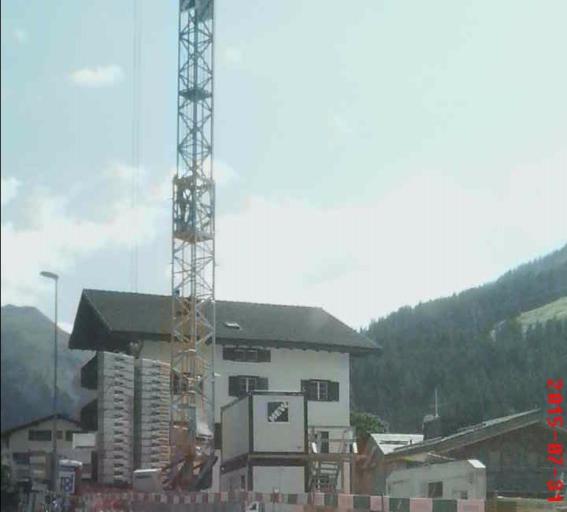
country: CH
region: Grisons
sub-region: Praettigau/Davos District
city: Klosters Serneus
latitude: 46.8778
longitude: 9.8795
